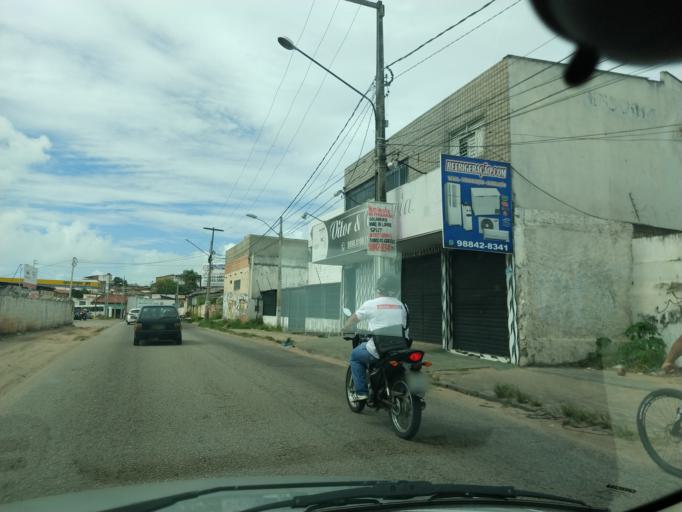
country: BR
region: Rio Grande do Norte
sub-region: Natal
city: Natal
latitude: -5.7981
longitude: -35.2387
